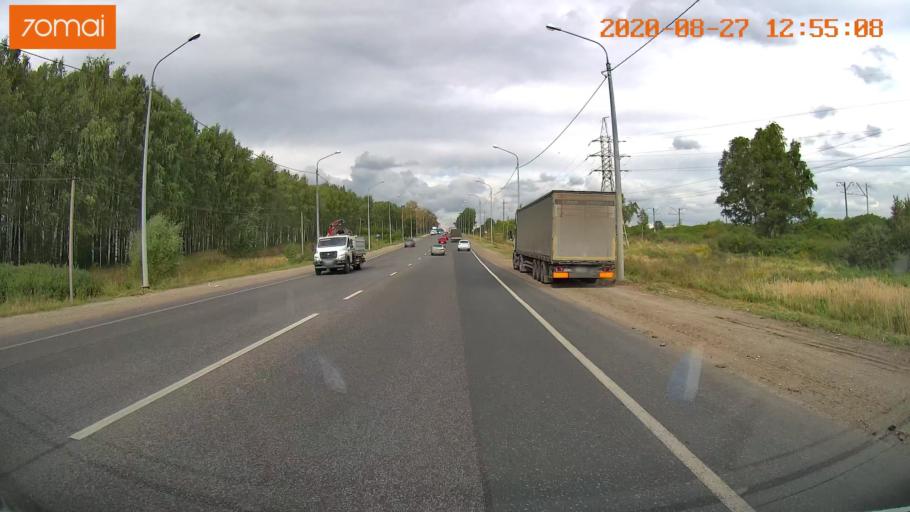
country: RU
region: Rjazan
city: Ryazan'
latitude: 54.6192
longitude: 39.6366
